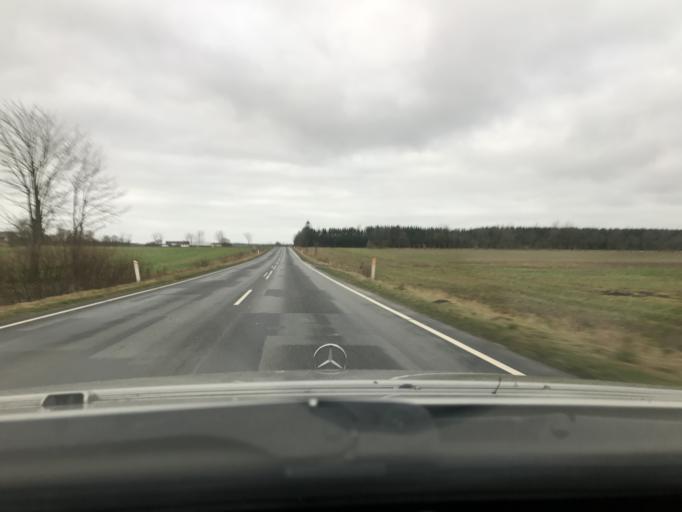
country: DK
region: South Denmark
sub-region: Tonder Kommune
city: Toftlund
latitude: 55.1782
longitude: 9.0245
